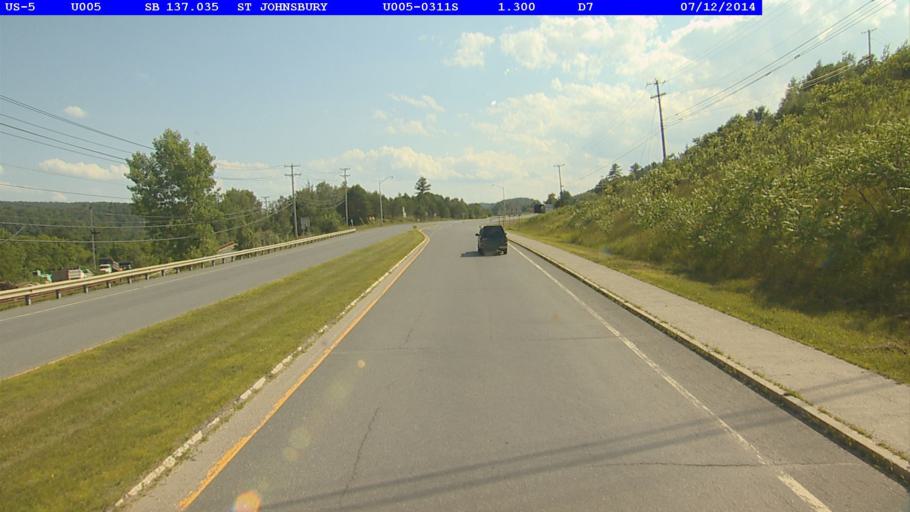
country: US
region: Vermont
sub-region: Caledonia County
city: Saint Johnsbury
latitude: 44.4121
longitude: -72.0180
